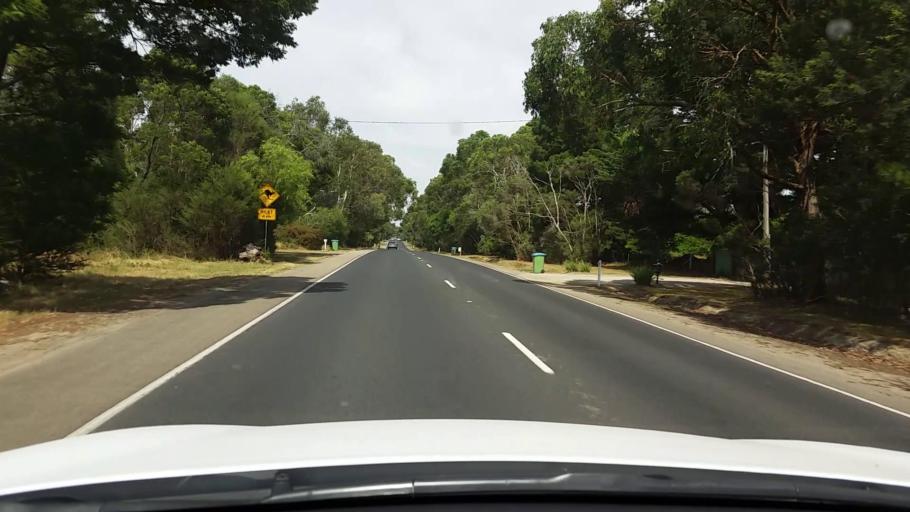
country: AU
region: Victoria
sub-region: Mornington Peninsula
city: Crib Point
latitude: -38.3463
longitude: 145.1658
